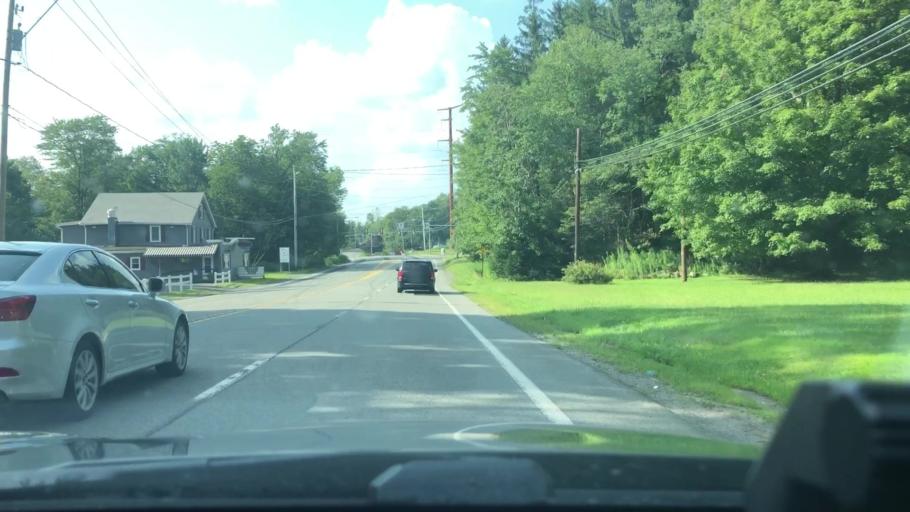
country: US
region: Pennsylvania
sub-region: Lackawanna County
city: Moscow
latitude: 41.2580
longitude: -75.5050
